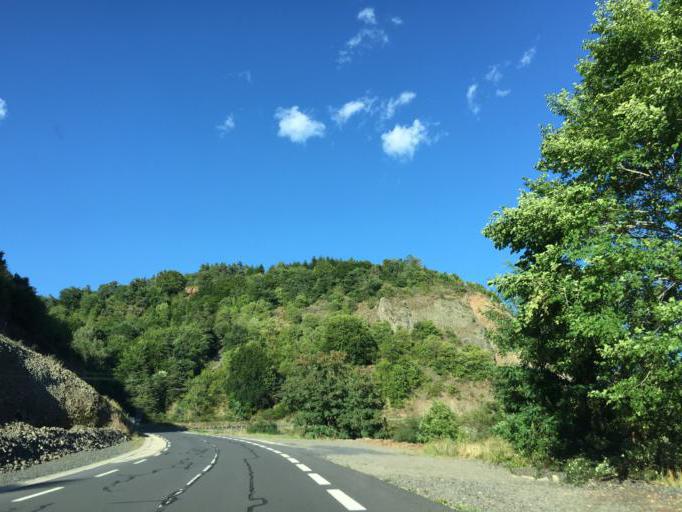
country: FR
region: Auvergne
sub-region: Departement de la Haute-Loire
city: Saugues
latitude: 44.9705
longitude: 3.6584
